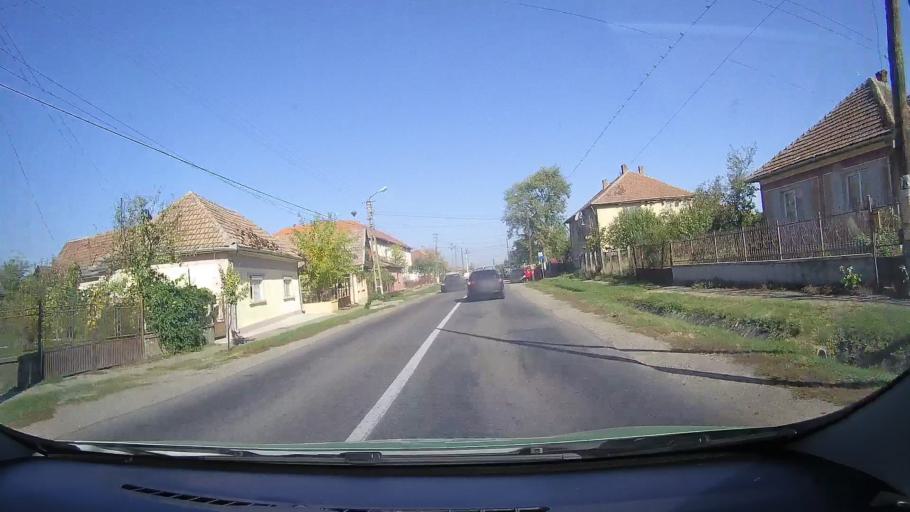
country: RO
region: Satu Mare
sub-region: Comuna Cauas
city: Cauas
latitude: 47.5678
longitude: 22.5454
